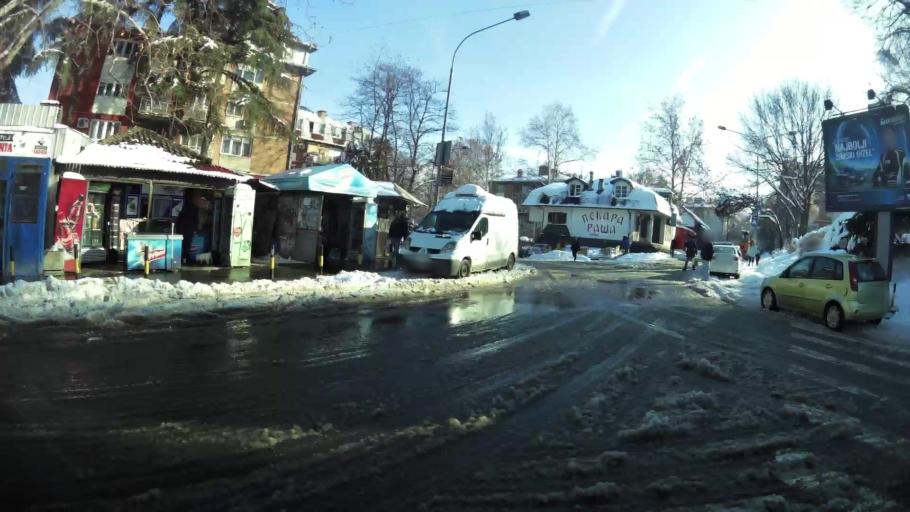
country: RS
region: Central Serbia
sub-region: Belgrade
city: Palilula
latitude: 44.8066
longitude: 20.5223
